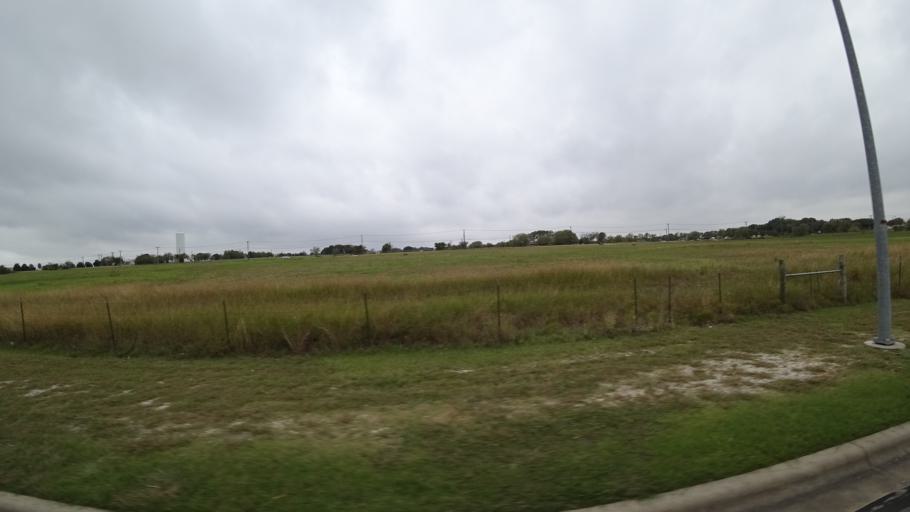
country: US
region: Texas
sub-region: Travis County
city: Pflugerville
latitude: 30.4561
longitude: -97.6099
